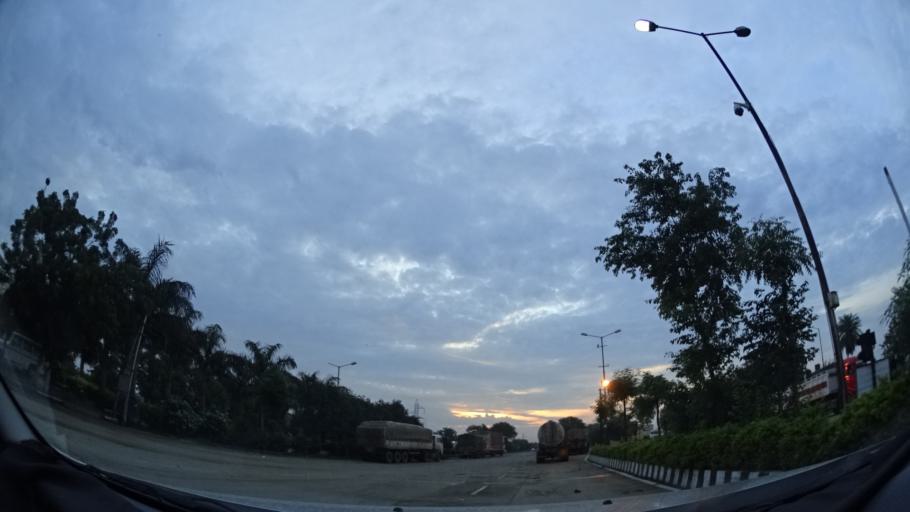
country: IN
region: Madhya Pradesh
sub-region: Dewas
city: Dewas
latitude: 22.9755
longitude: 76.2217
